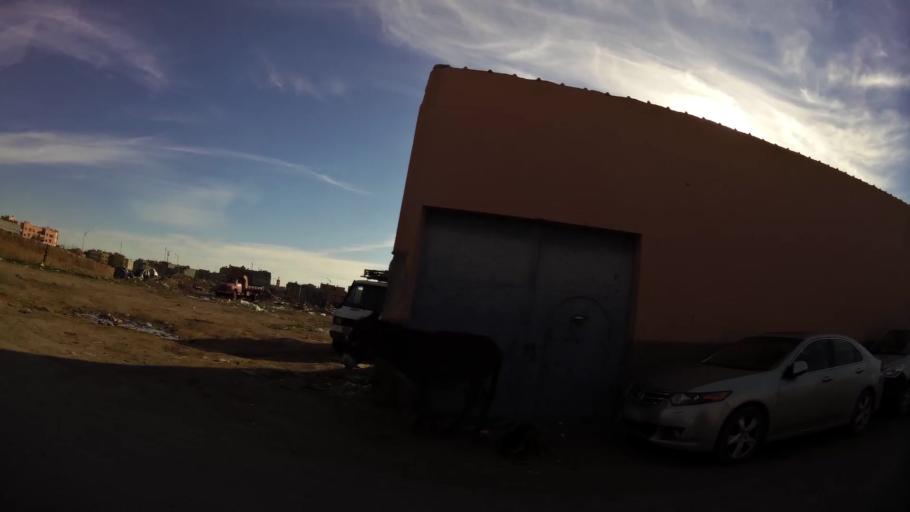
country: MA
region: Marrakech-Tensift-Al Haouz
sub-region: Marrakech
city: Marrakesh
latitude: 31.6836
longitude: -8.0565
